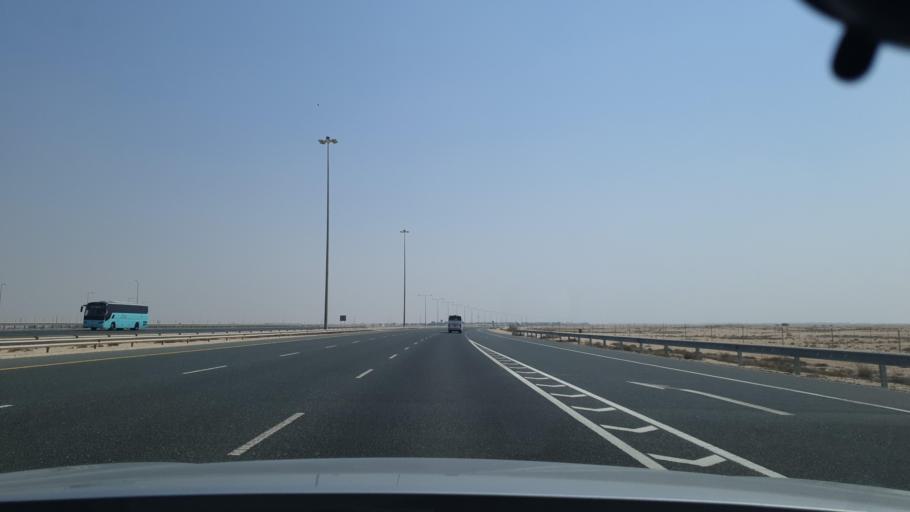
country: QA
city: Al Ghuwayriyah
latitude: 25.8267
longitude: 51.3563
